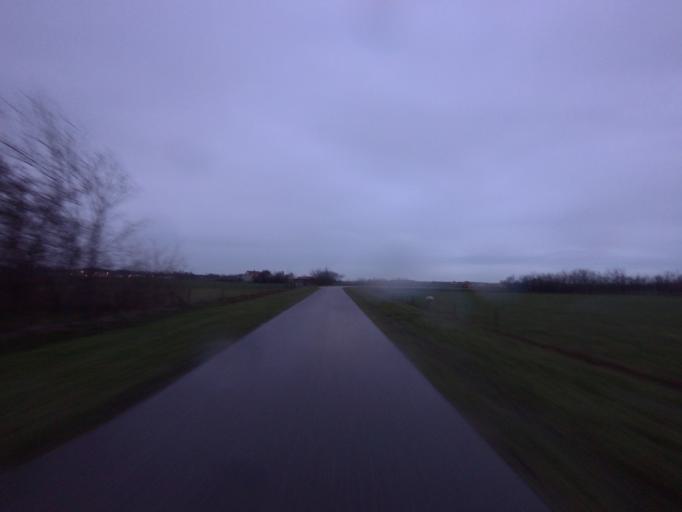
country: NL
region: North Holland
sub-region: Gemeente Texel
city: Den Burg
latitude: 53.0666
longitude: 4.7981
